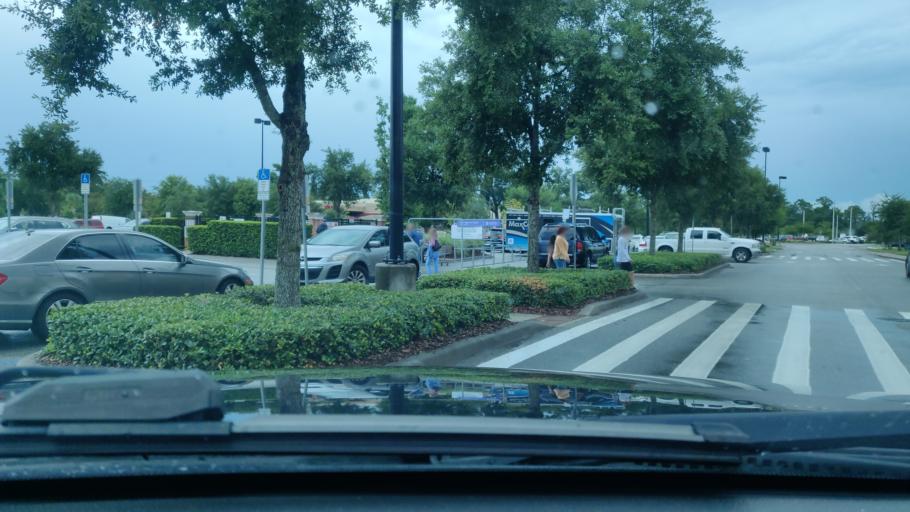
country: US
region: Florida
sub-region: Volusia County
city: Port Orange
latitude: 29.1088
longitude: -81.0243
